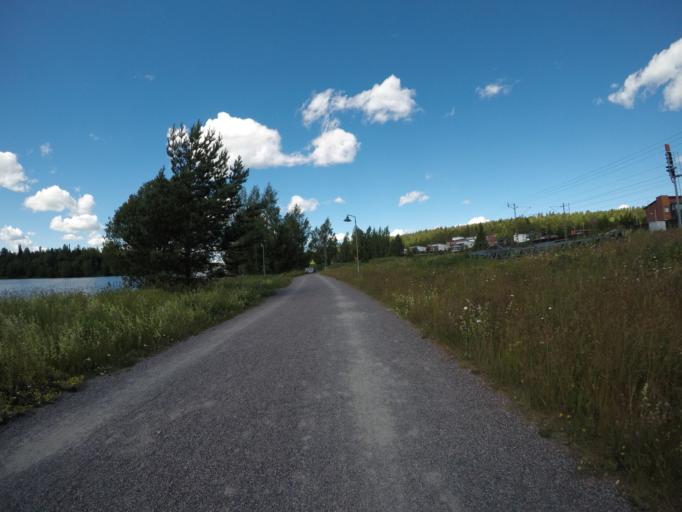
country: FI
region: Haeme
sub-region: Haemeenlinna
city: Haemeenlinna
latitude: 61.0094
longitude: 24.4625
